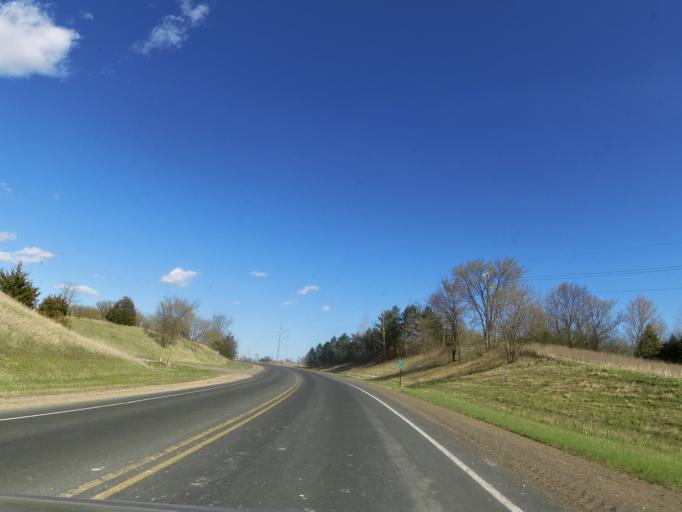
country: US
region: Wisconsin
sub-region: Saint Croix County
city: North Hudson
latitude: 45.0361
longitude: -92.6817
